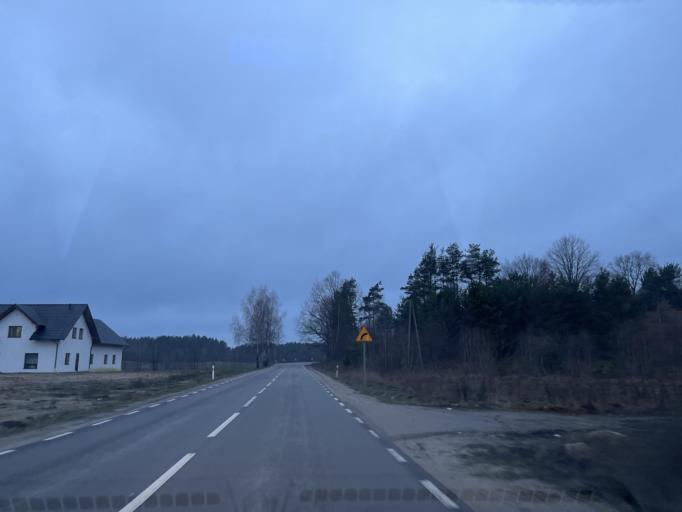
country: PL
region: Pomeranian Voivodeship
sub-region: Powiat wejherowski
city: Szemud
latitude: 54.4161
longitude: 18.1958
